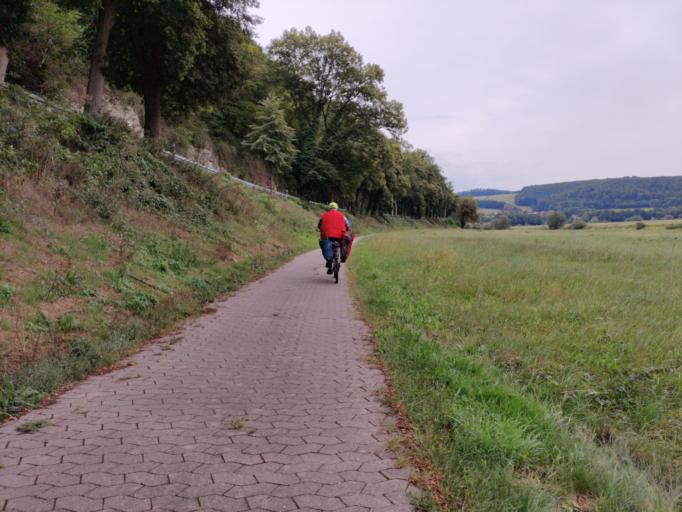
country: DE
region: Lower Saxony
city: Pegestorf
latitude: 51.9113
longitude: 9.4679
